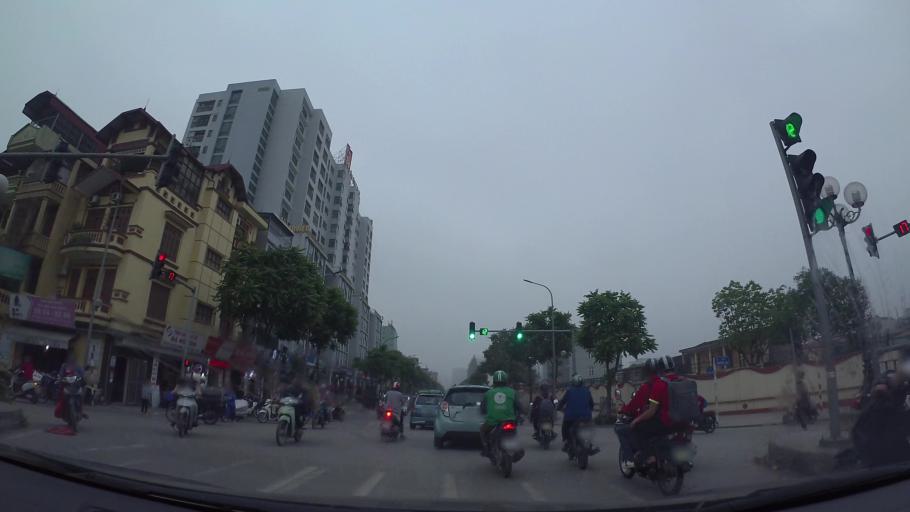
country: VN
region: Ha Noi
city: Hai BaTrung
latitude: 20.9872
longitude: 105.8358
